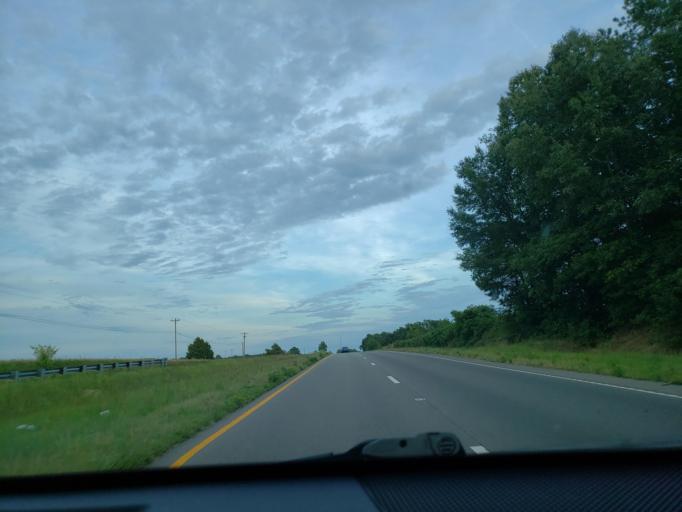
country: US
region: Virginia
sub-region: City of Emporia
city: Emporia
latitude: 36.7248
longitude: -77.5959
